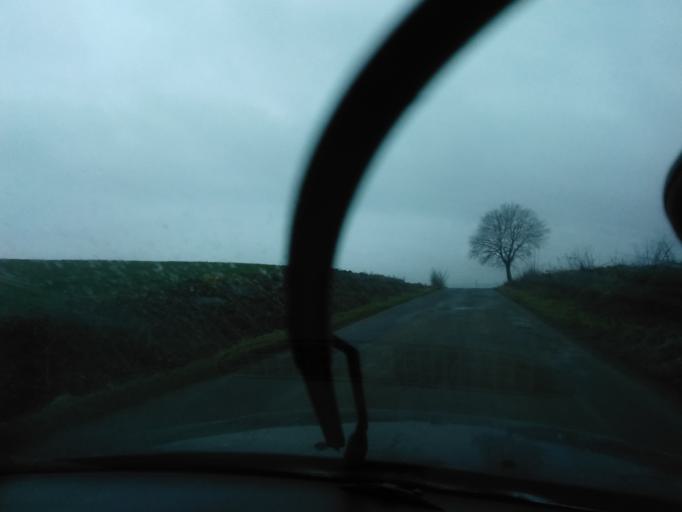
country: PL
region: Subcarpathian Voivodeship
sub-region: Powiat jaroslawski
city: Rokietnica
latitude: 49.9120
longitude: 22.6108
